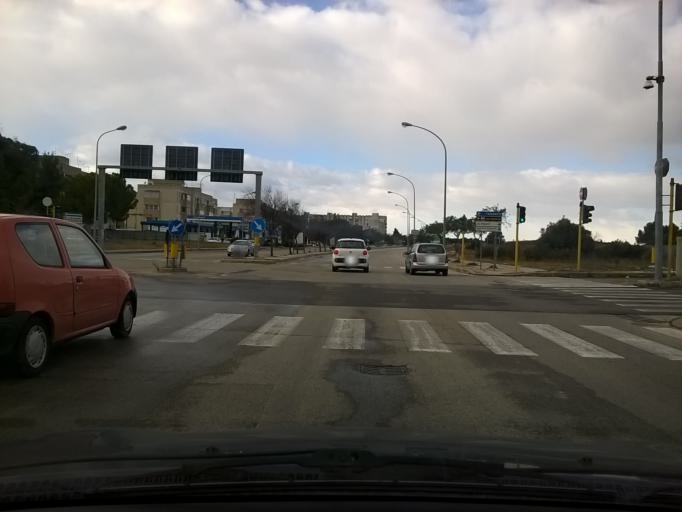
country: IT
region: Apulia
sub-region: Provincia di Taranto
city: Paolo VI
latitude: 40.5195
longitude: 17.2679
